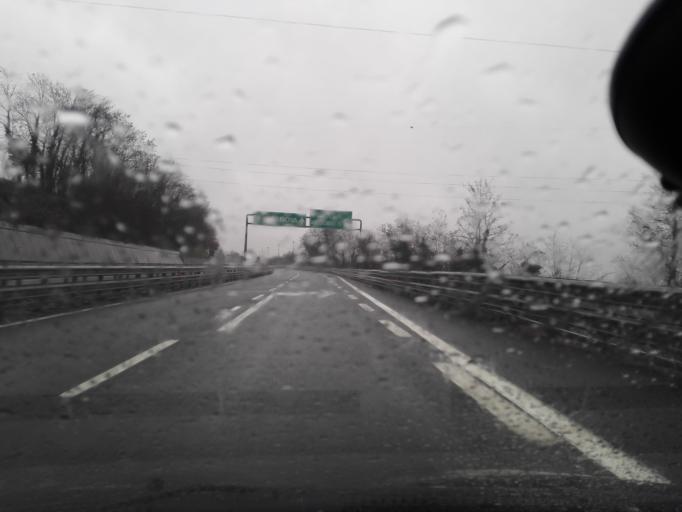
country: IT
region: Piedmont
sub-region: Provincia di Alessandria
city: Vignole Borbera
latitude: 44.7042
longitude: 8.8826
